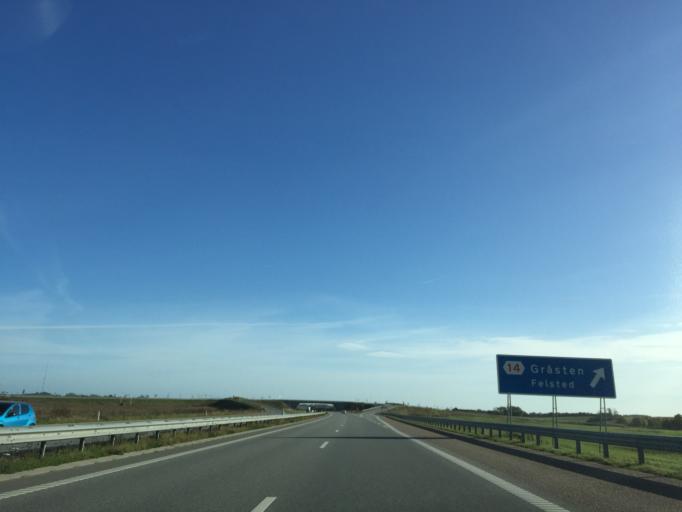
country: DK
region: South Denmark
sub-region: Sonderborg Kommune
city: Grasten
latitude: 54.9522
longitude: 9.5100
